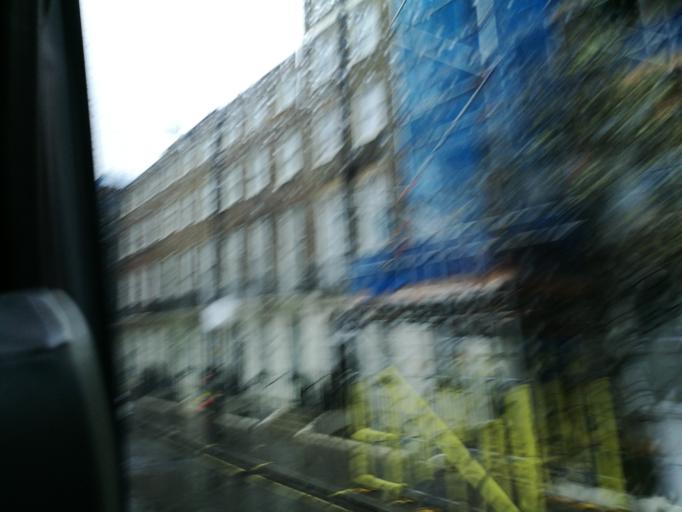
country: GB
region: England
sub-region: Greater London
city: Camden Town
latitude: 51.5183
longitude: -0.1579
